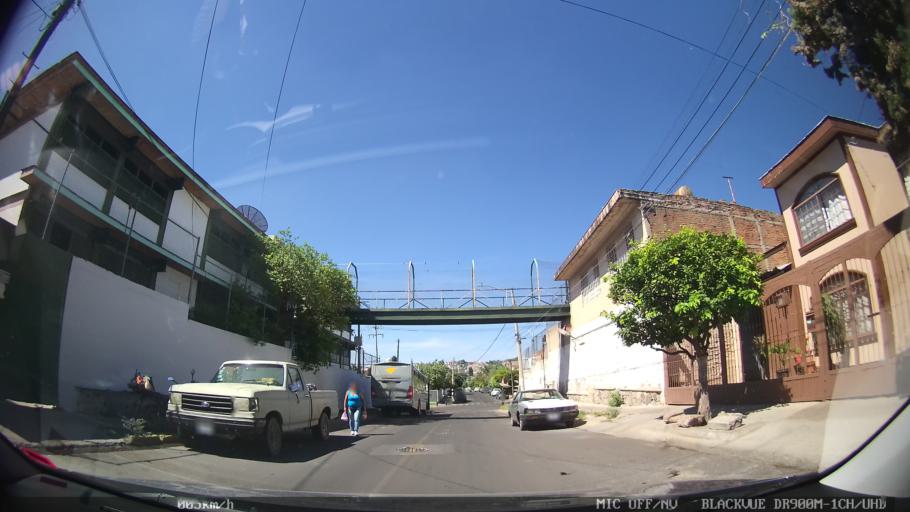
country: MX
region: Jalisco
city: Tlaquepaque
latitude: 20.6970
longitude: -103.2869
